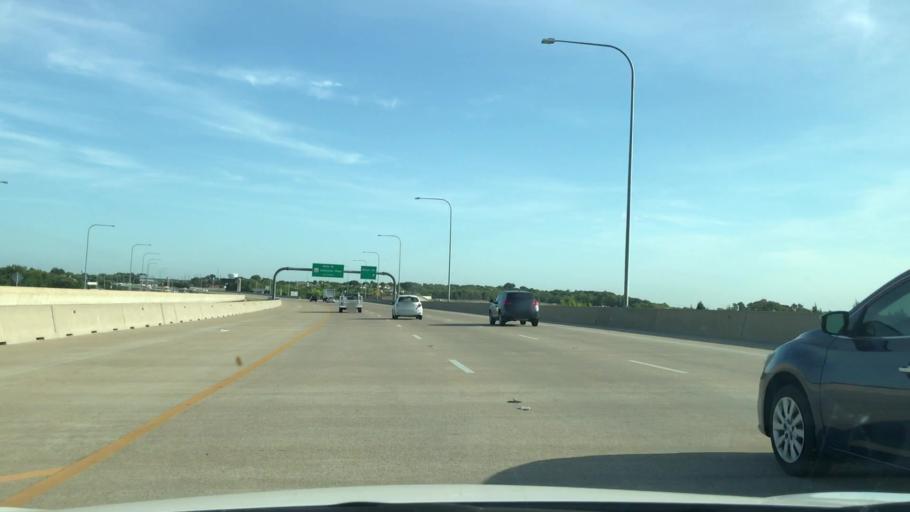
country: US
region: Texas
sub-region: Dallas County
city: Rowlett
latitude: 32.8741
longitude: -96.5523
